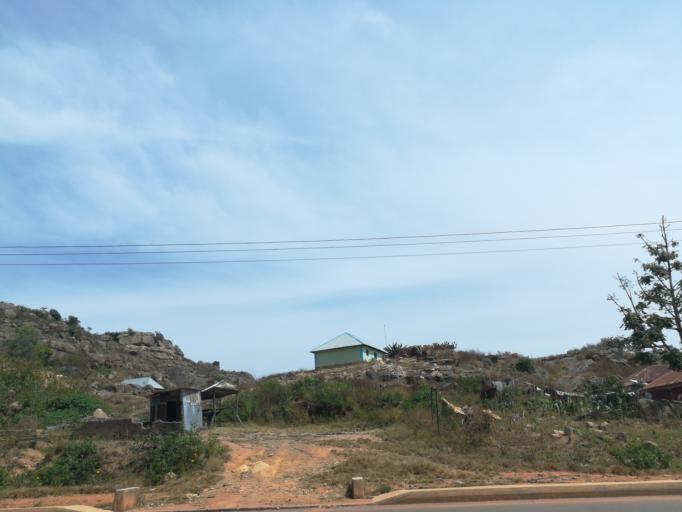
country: NG
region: Plateau
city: Bukuru
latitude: 9.8297
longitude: 8.8669
